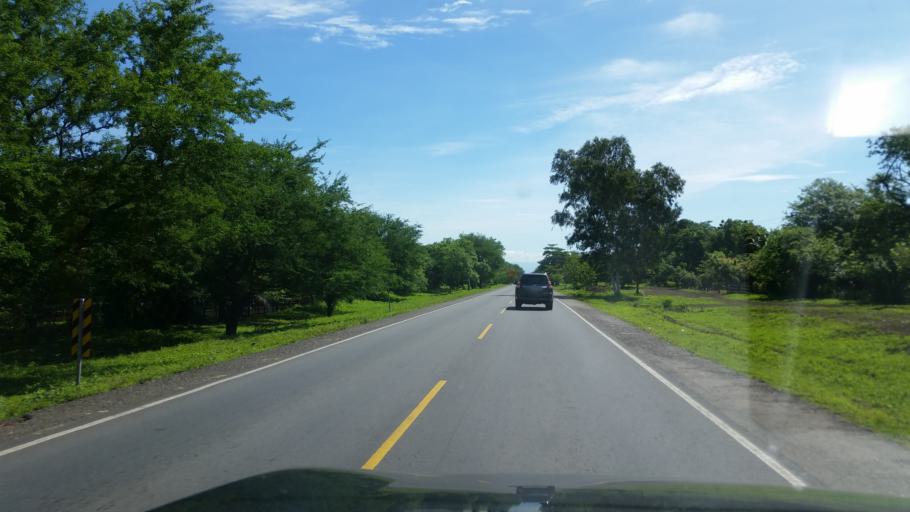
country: NI
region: Chinandega
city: El Viejo
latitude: 12.7537
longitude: -87.0661
